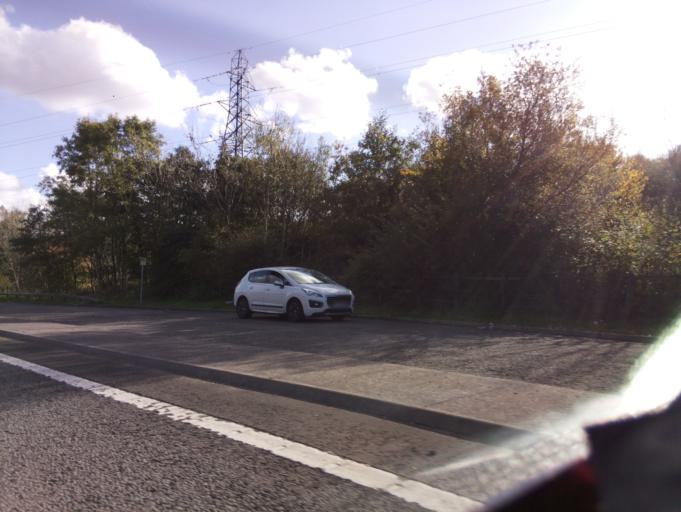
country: GB
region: Wales
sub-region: Merthyr Tydfil County Borough
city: Merthyr Tydfil
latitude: 51.7575
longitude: -3.4051
